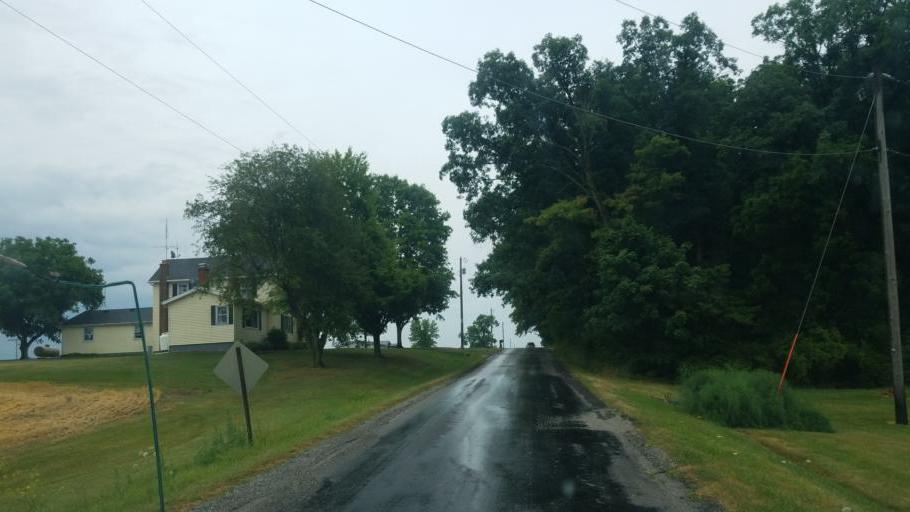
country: US
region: Ohio
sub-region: Williams County
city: Edgerton
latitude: 41.4248
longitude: -84.6704
